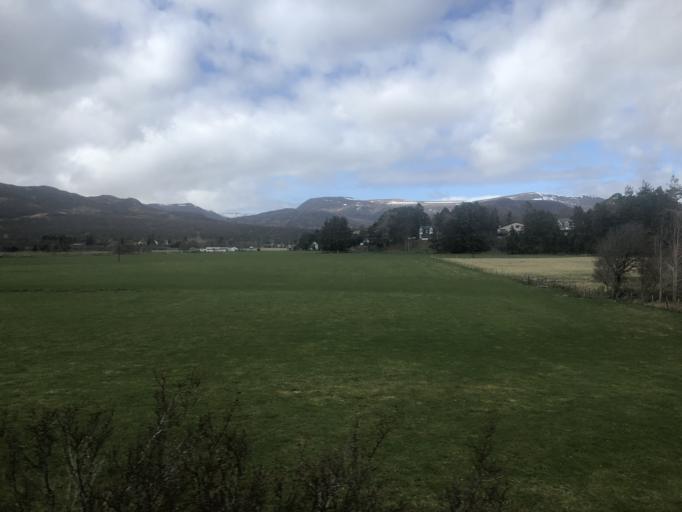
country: GB
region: Scotland
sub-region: Highland
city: Kingussie
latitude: 57.0577
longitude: -4.1212
